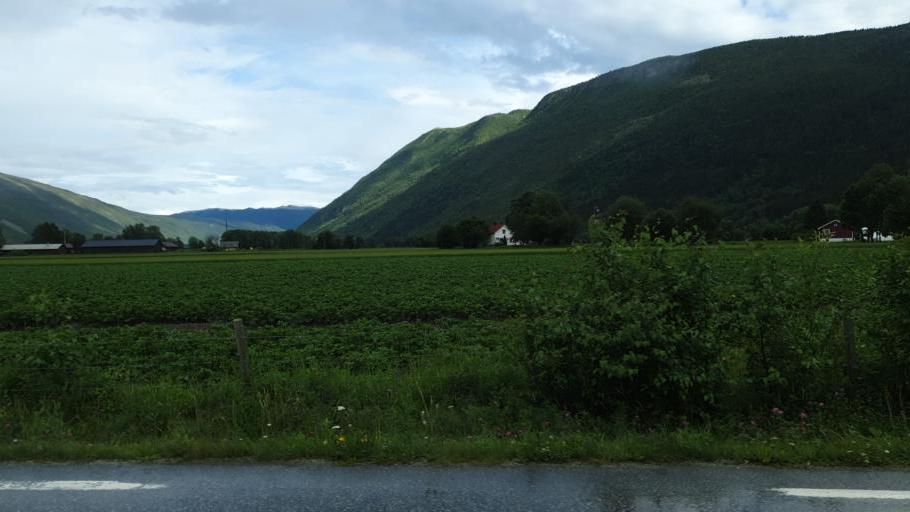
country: NO
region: Oppland
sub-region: Sel
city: Otta
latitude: 61.8464
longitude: 9.4168
